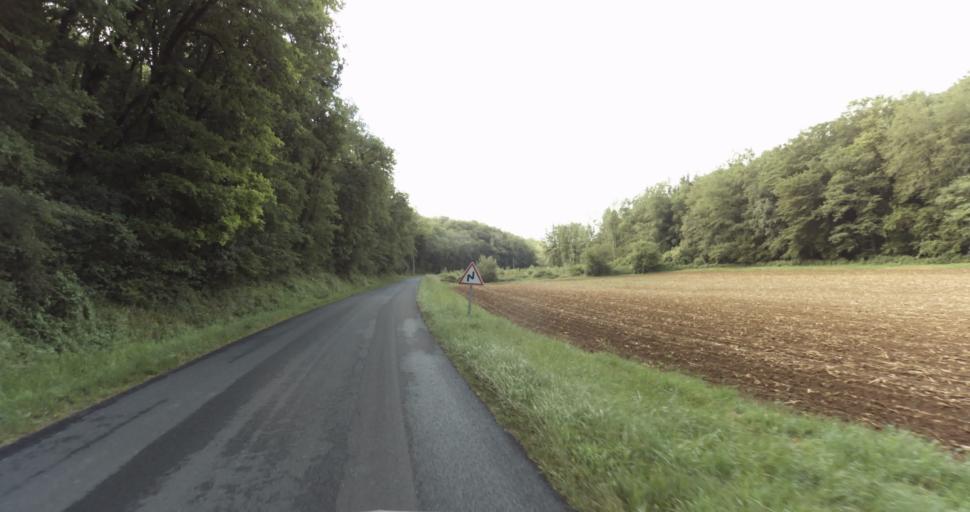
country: FR
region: Aquitaine
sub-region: Departement de la Dordogne
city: Lalinde
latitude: 44.8632
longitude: 0.7744
